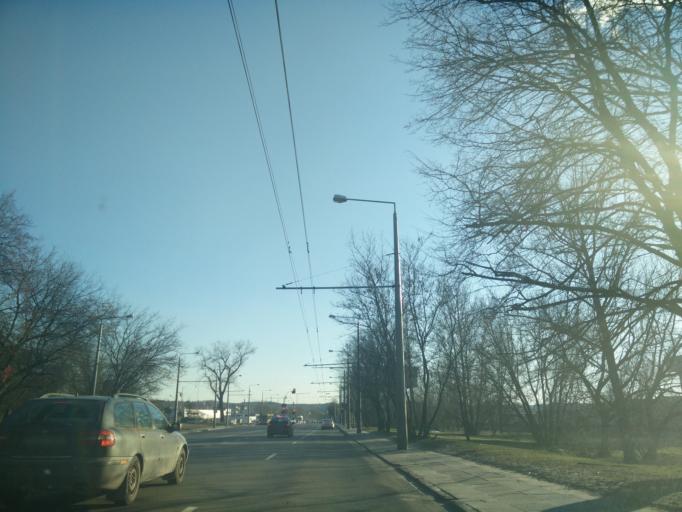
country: LT
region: Vilnius County
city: Vilkpede
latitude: 54.6650
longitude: 25.2366
